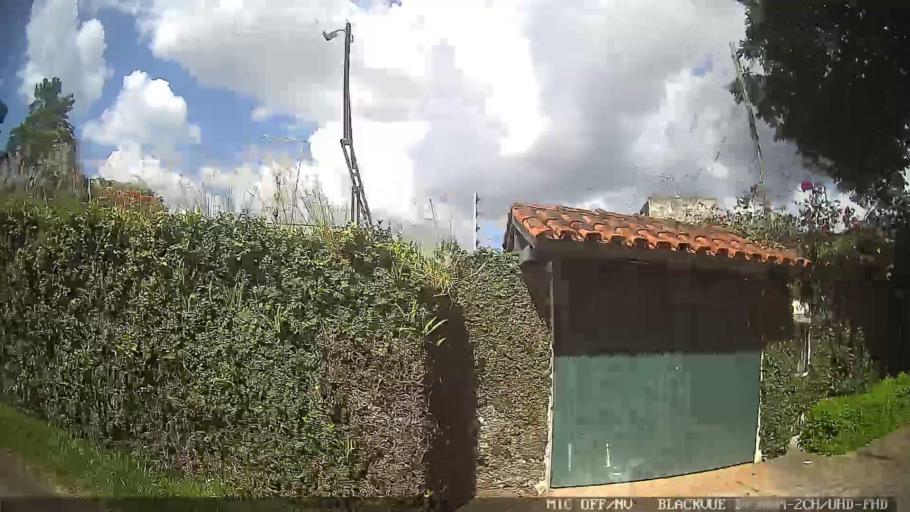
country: BR
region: Sao Paulo
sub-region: Atibaia
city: Atibaia
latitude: -23.1283
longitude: -46.5525
